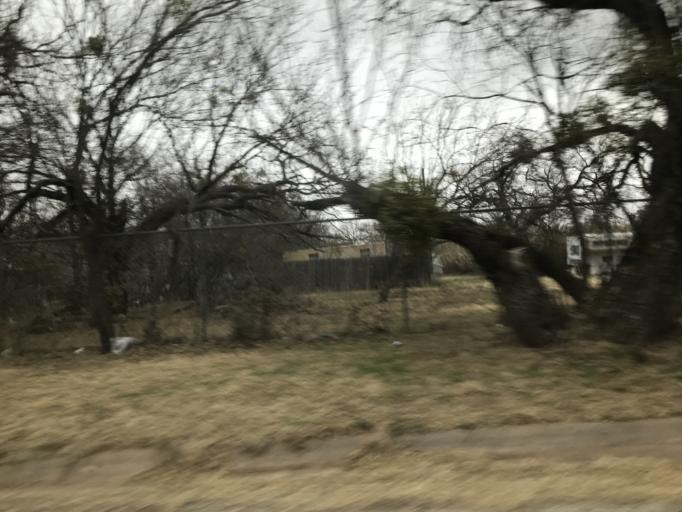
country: US
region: Texas
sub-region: Taylor County
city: Abilene
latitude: 32.4539
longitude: -99.7502
